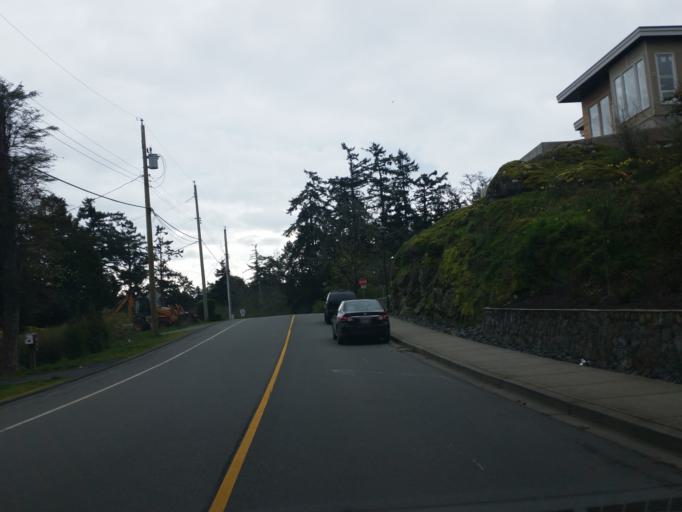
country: CA
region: British Columbia
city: Colwood
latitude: 48.4546
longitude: -123.4590
